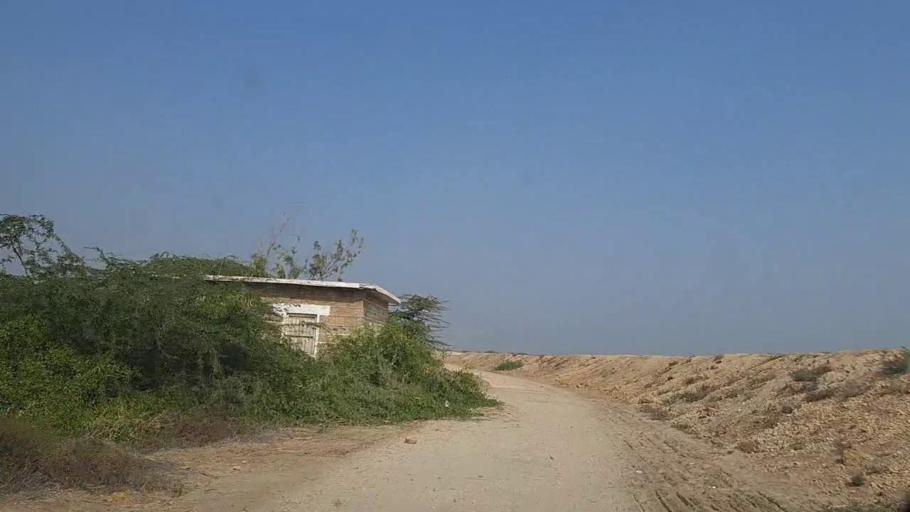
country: PK
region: Sindh
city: Thatta
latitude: 24.6560
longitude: 67.9267
